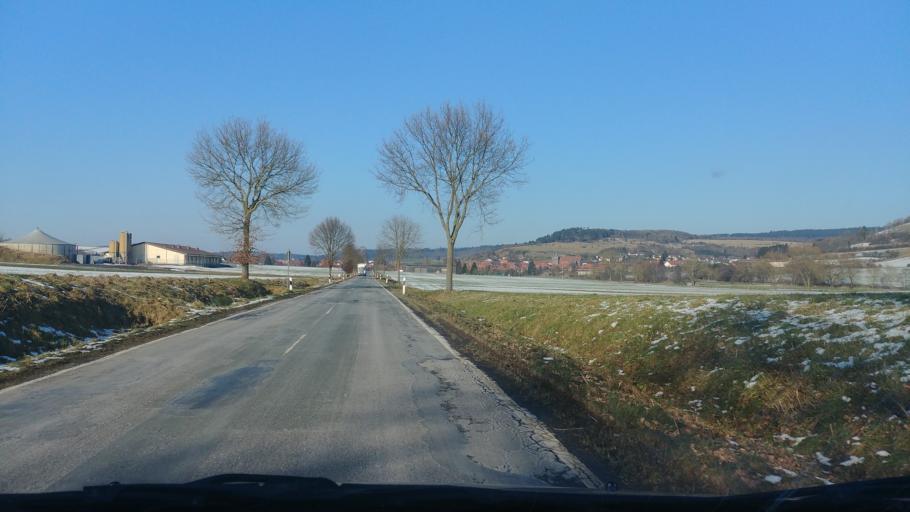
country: DE
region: Lower Saxony
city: Hardegsen
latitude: 51.7239
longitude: 9.7866
